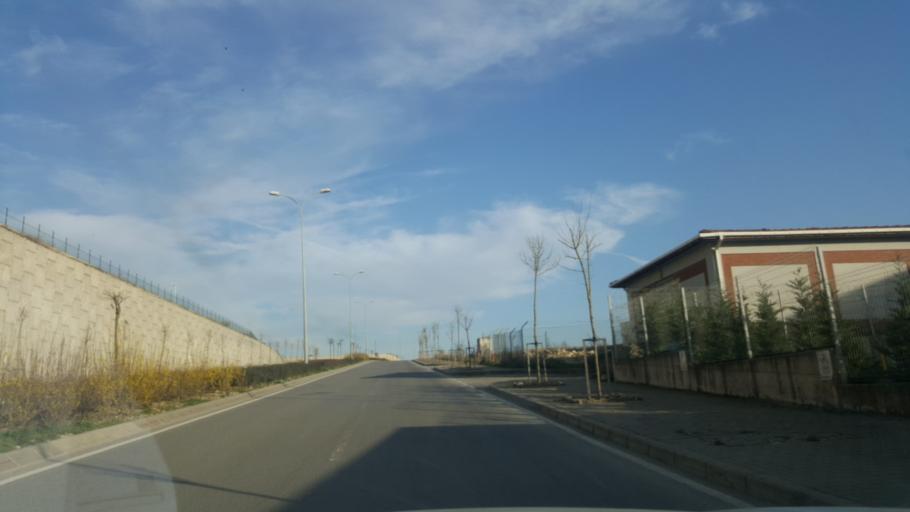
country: TR
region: Kocaeli
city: Tavsanli
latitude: 40.8321
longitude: 29.5552
